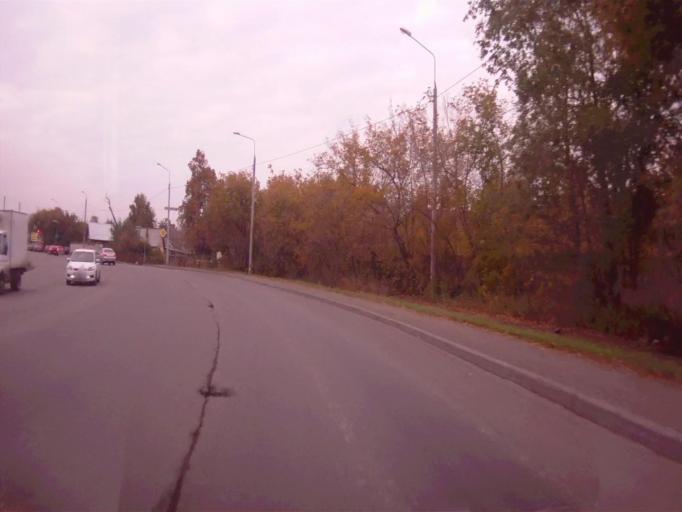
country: RU
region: Chelyabinsk
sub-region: Gorod Chelyabinsk
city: Chelyabinsk
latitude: 55.1333
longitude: 61.3852
